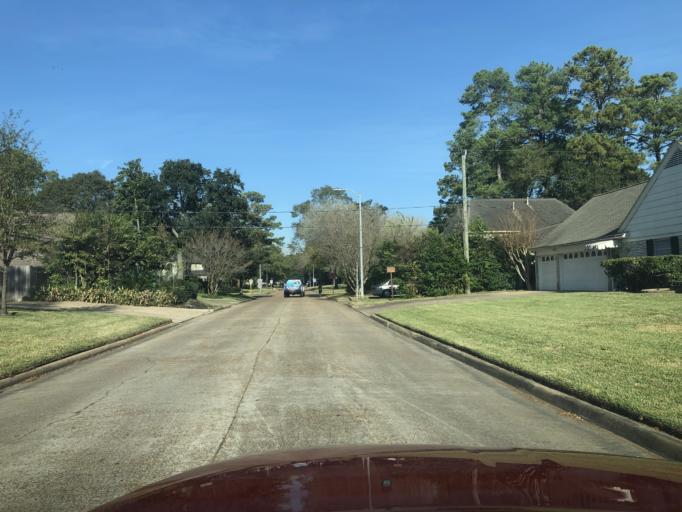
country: US
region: Texas
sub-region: Harris County
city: Spring
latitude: 30.0138
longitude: -95.4621
